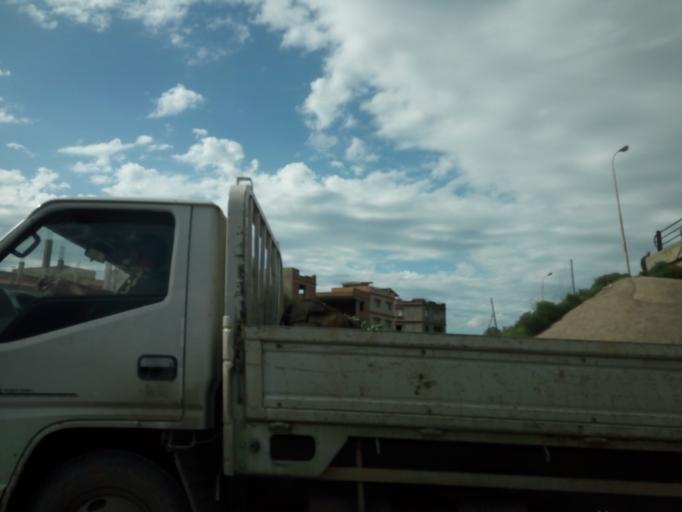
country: DZ
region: Blida
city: Chiffa
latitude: 36.4540
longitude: 2.7394
